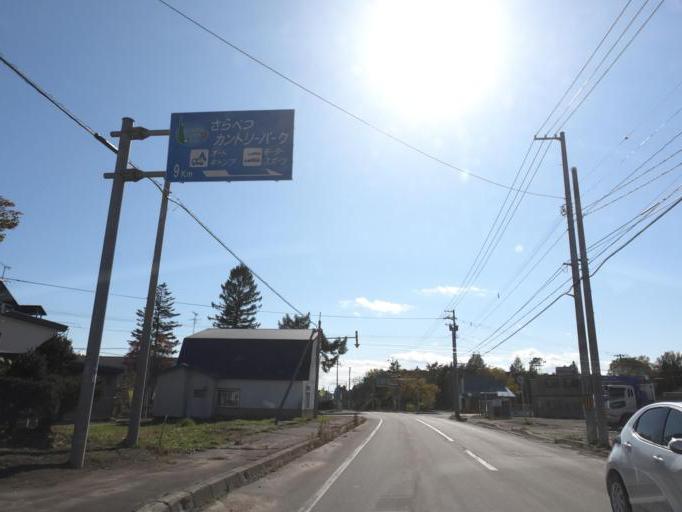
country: JP
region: Hokkaido
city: Obihiro
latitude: 42.6756
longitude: 143.3112
